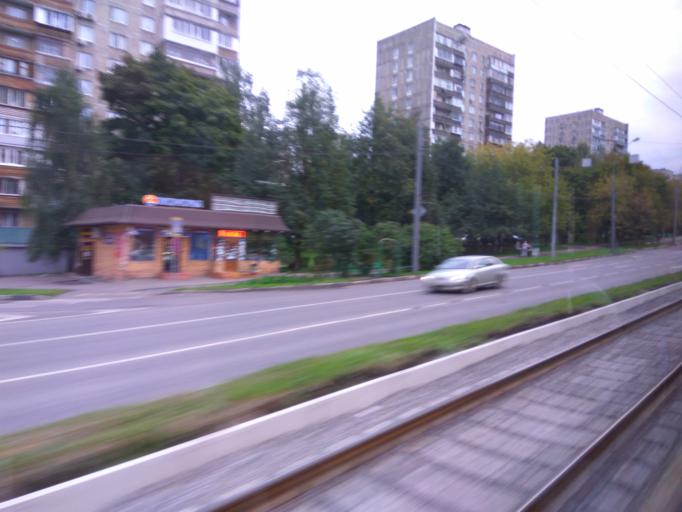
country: RU
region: Moscow
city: Chertanovo Yuzhnoye
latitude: 55.6048
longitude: 37.5899
